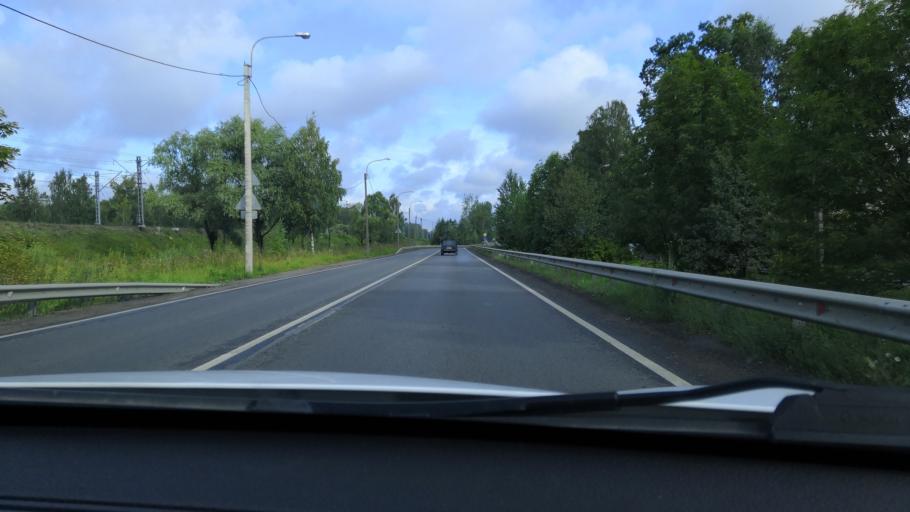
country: RU
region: St.-Petersburg
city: Tyarlevo
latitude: 59.7034
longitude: 30.4393
